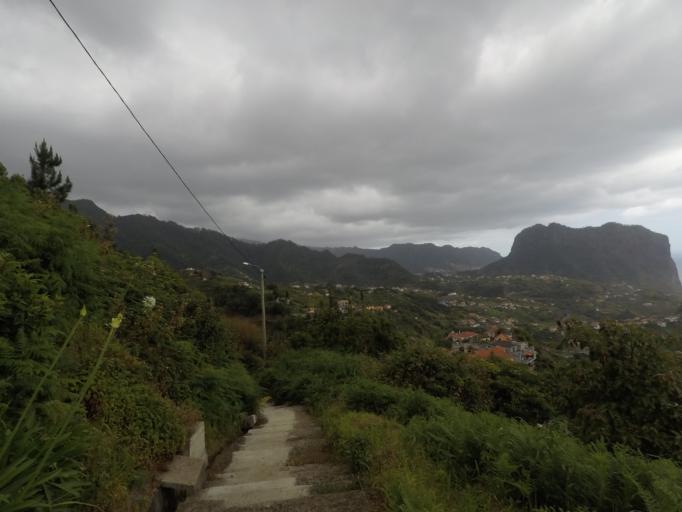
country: PT
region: Madeira
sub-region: Santa Cruz
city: Santa Cruz
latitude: 32.7519
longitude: -16.8256
